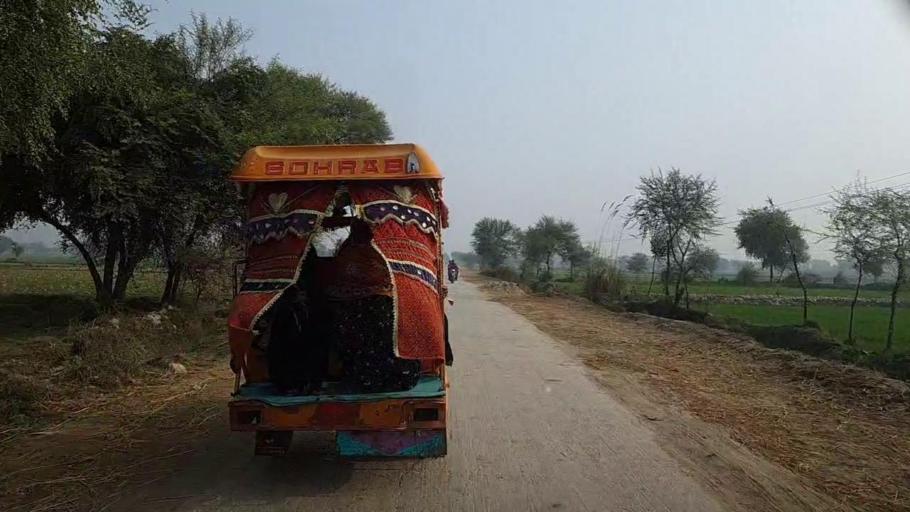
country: PK
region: Sindh
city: Dadu
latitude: 26.8354
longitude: 67.7729
